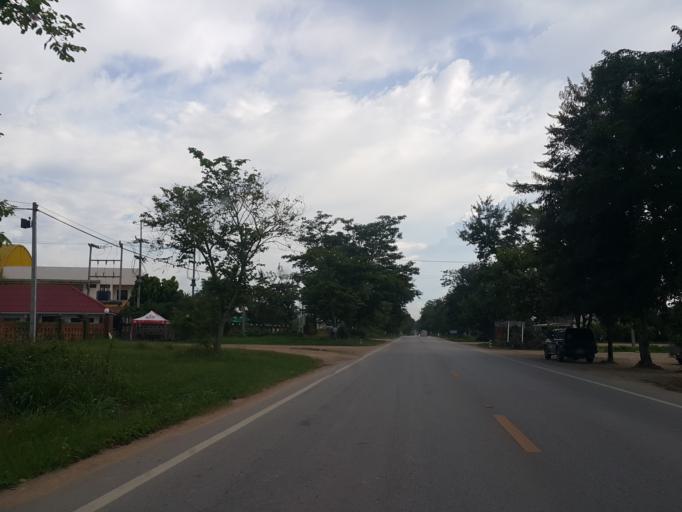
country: TH
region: Chiang Mai
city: Phrao
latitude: 19.3112
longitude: 99.1901
